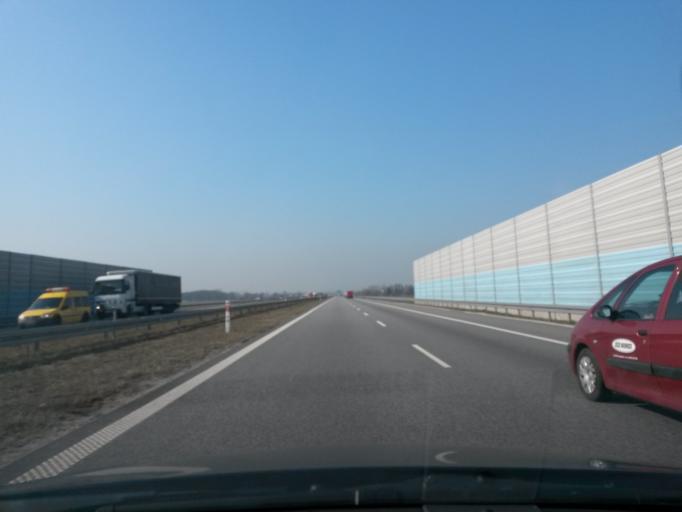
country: PL
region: Lodz Voivodeship
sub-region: powiat Lowicki
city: Lyszkowice
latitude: 51.9997
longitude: 19.9331
